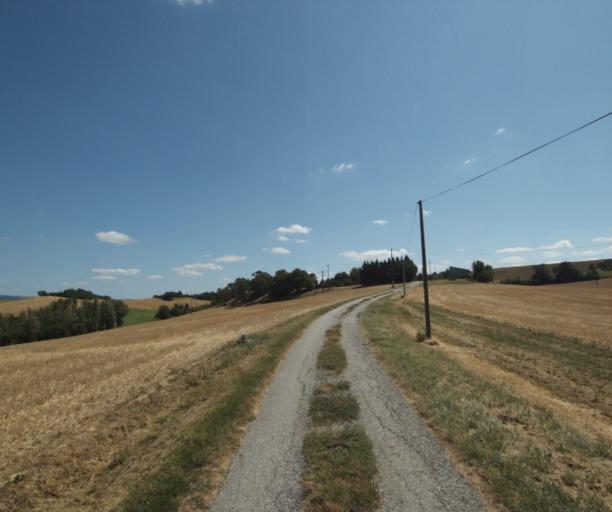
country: FR
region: Midi-Pyrenees
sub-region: Departement de la Haute-Garonne
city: Saint-Felix-Lauragais
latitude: 43.4610
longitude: 1.8848
